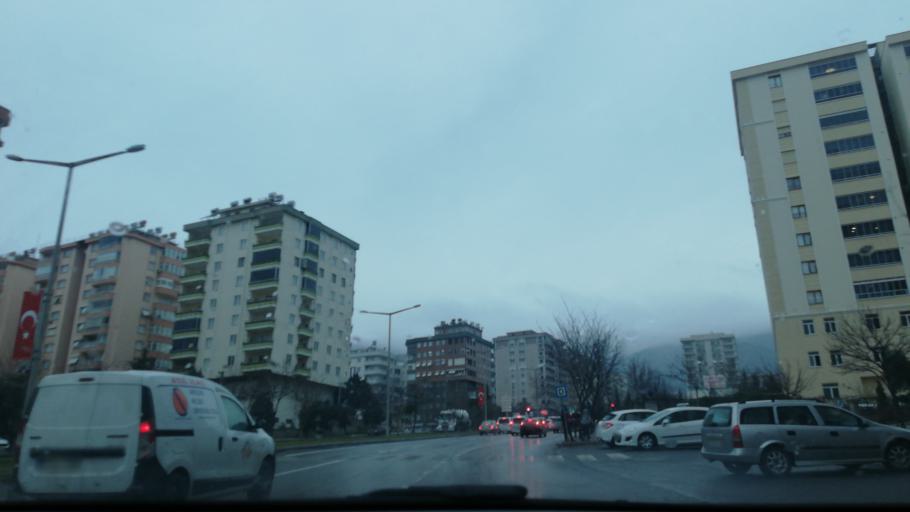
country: TR
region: Kahramanmaras
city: Kahramanmaras
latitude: 37.5870
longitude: 36.8876
